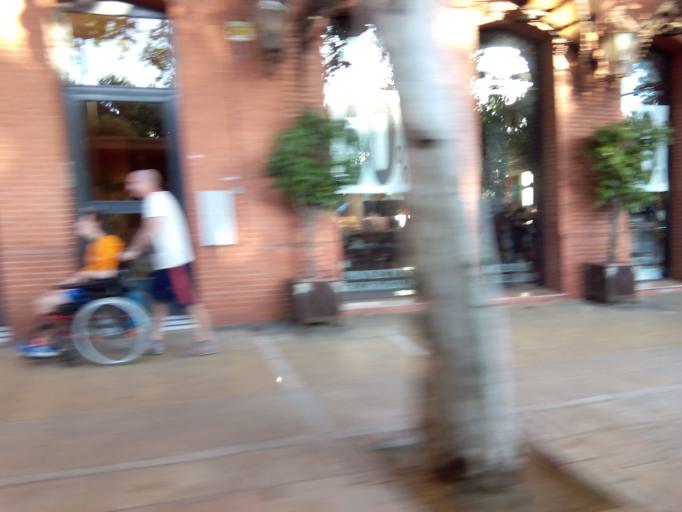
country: ES
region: Andalusia
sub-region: Provincia de Sevilla
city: Sevilla
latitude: 37.3976
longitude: -6.0011
